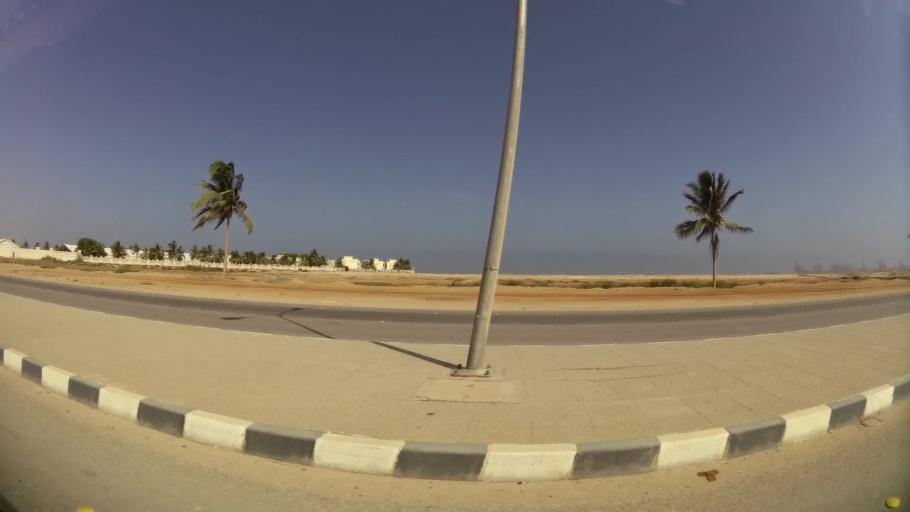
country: OM
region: Zufar
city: Salalah
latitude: 16.9882
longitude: 54.0223
